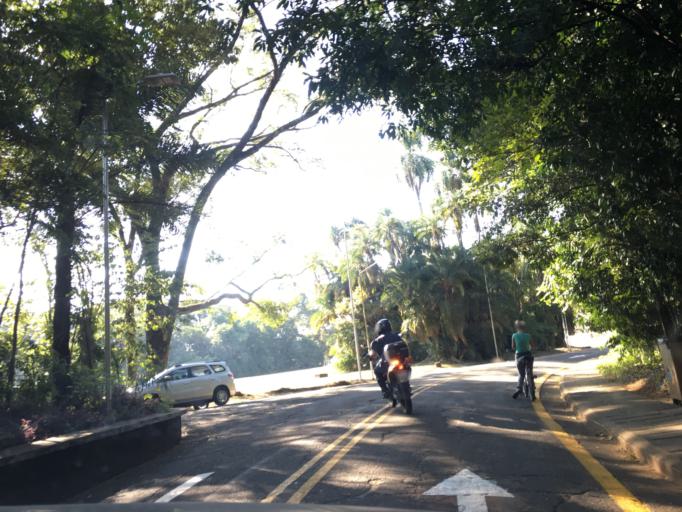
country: BR
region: Sao Paulo
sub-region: Piracicaba
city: Piracicaba
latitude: -22.7110
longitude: -47.6319
